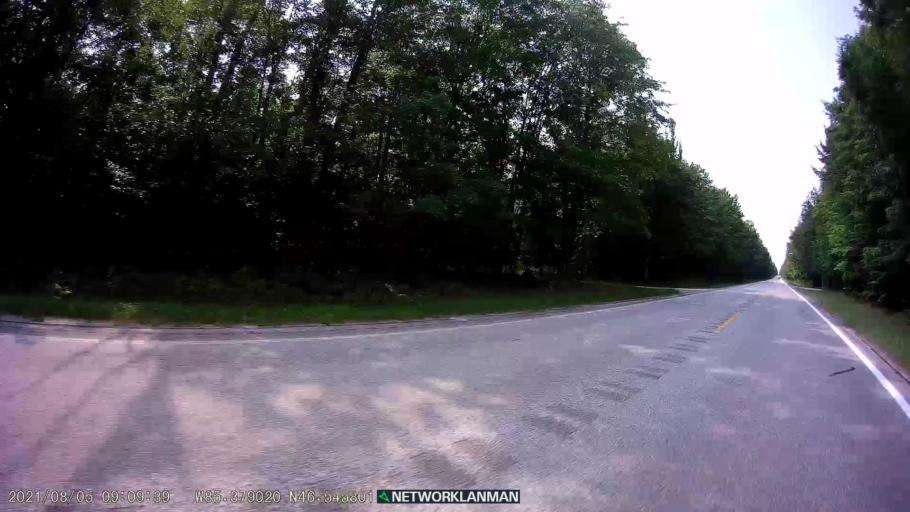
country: US
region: Michigan
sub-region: Luce County
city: Newberry
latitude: 46.5456
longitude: -85.3793
